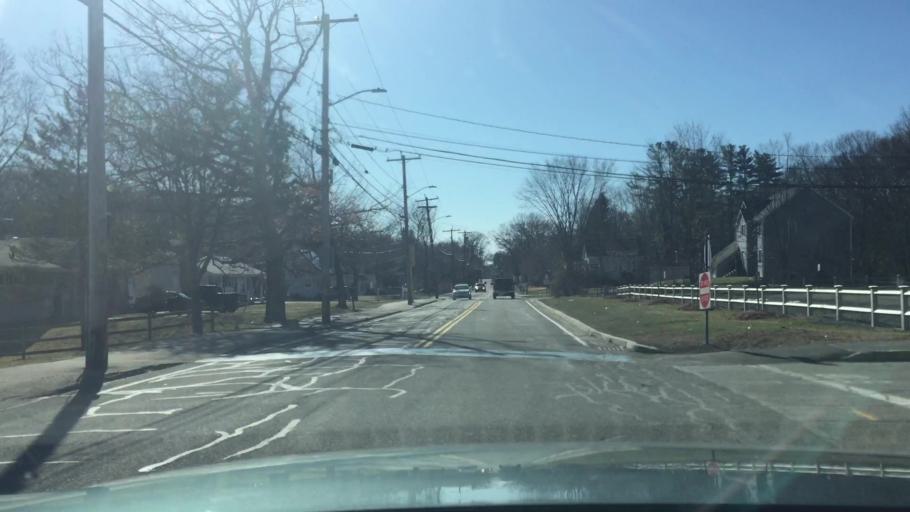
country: US
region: Massachusetts
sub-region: Norfolk County
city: Medway
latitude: 42.1461
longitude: -71.4060
